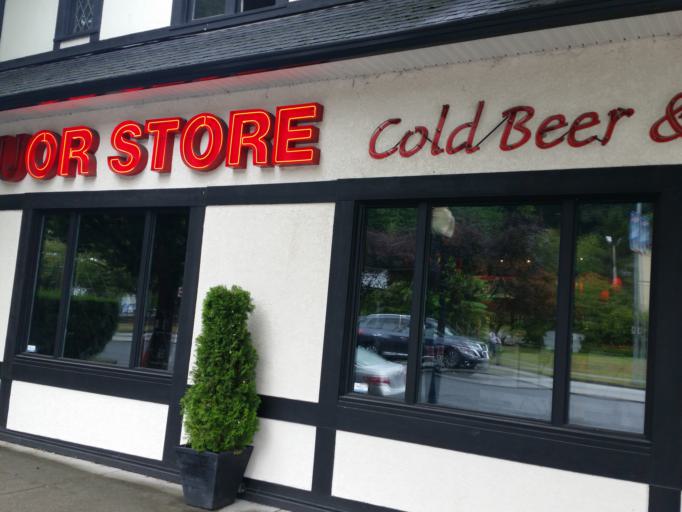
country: CA
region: British Columbia
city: Port Moody
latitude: 49.2768
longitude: -122.8571
